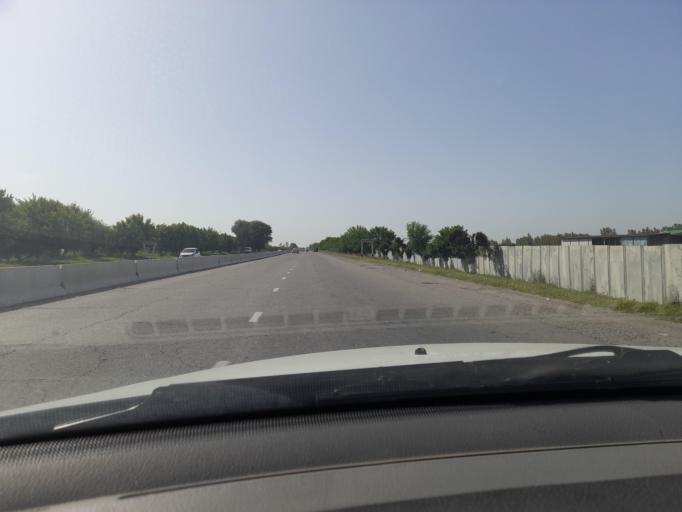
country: UZ
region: Samarqand
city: Chelak
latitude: 39.8417
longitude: 66.8170
